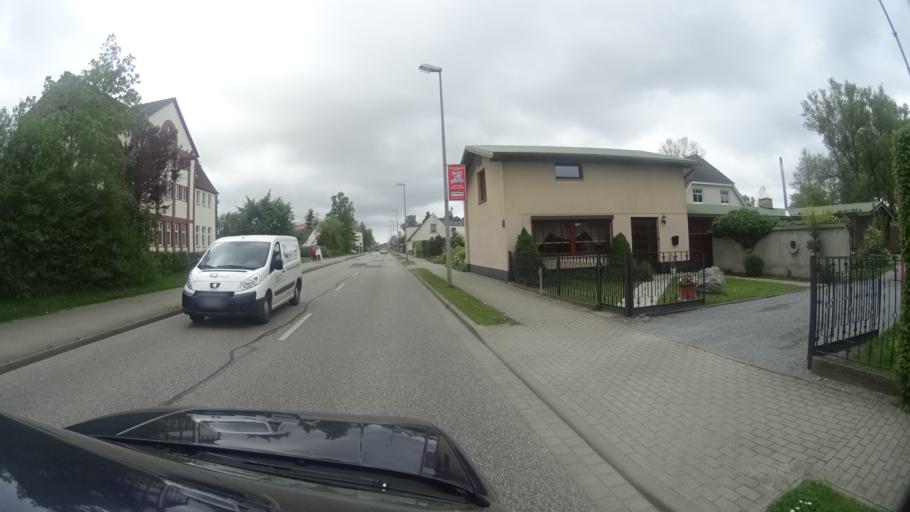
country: DE
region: Mecklenburg-Vorpommern
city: Ribnitz-Damgarten
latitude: 54.2464
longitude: 12.4129
